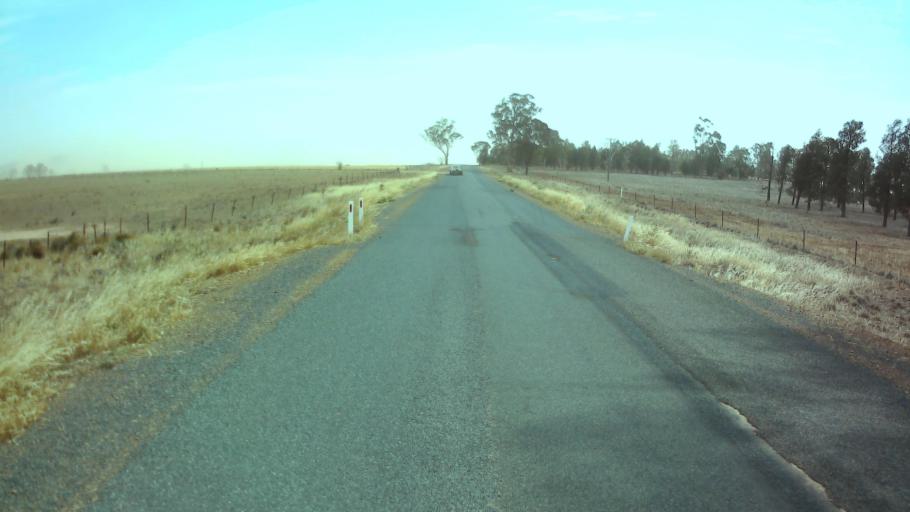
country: AU
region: New South Wales
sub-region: Weddin
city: Grenfell
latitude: -33.7493
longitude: 147.9911
